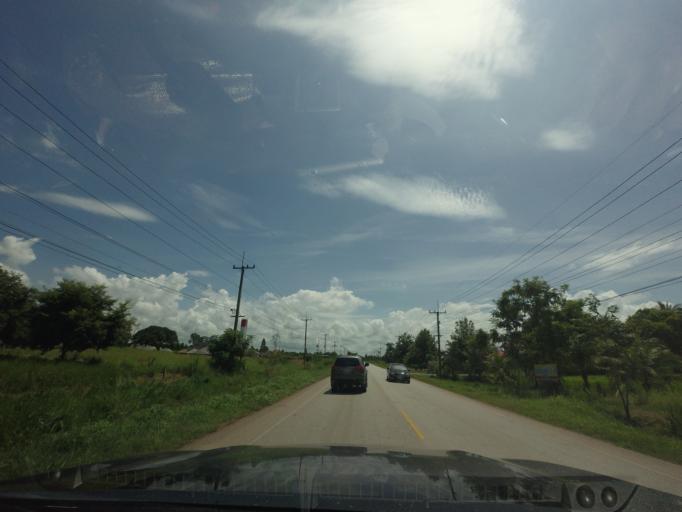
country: TH
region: Changwat Udon Thani
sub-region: Amphoe Ban Phue
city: Ban Phue
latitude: 17.7096
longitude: 102.4205
